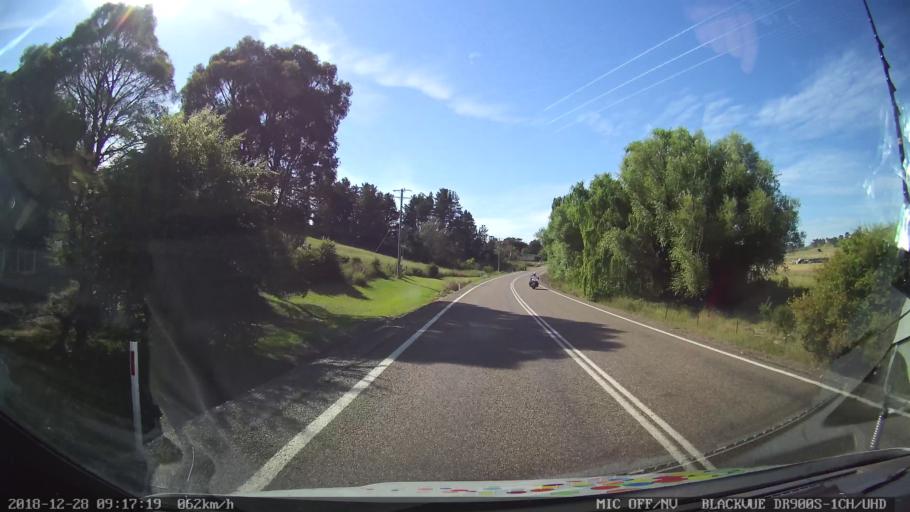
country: AU
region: New South Wales
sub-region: Upper Lachlan Shire
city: Crookwell
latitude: -34.3190
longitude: 149.3603
